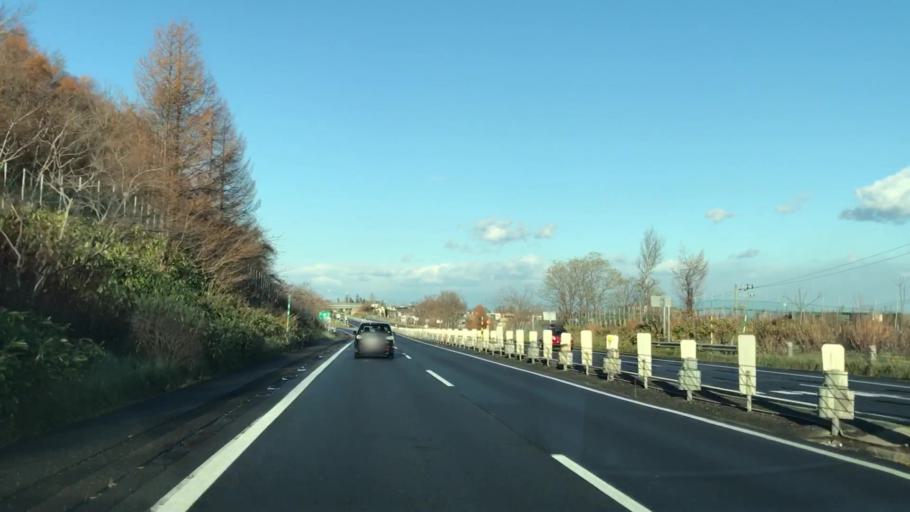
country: JP
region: Hokkaido
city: Sapporo
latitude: 43.1213
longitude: 141.2180
